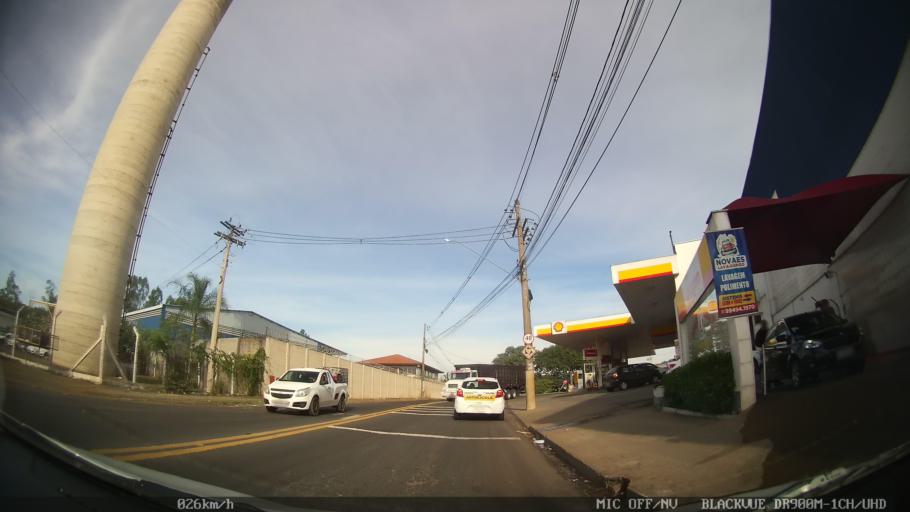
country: BR
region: Sao Paulo
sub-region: Piracicaba
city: Piracicaba
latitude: -22.6998
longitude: -47.6749
